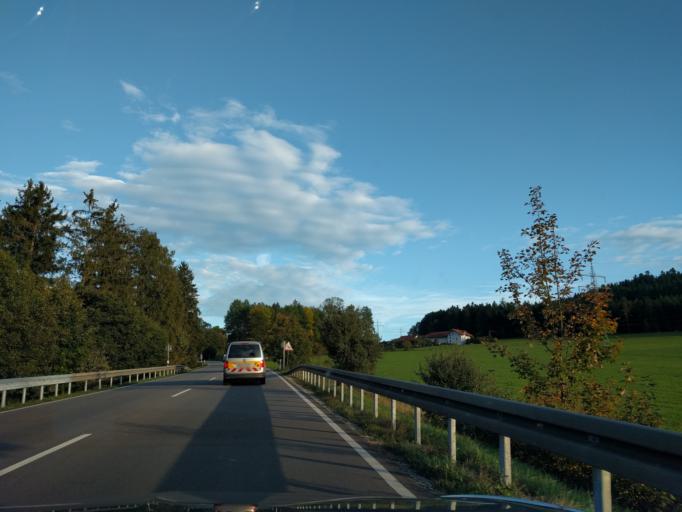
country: DE
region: Bavaria
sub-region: Lower Bavaria
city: Geiersthal
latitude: 49.0370
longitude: 12.9503
